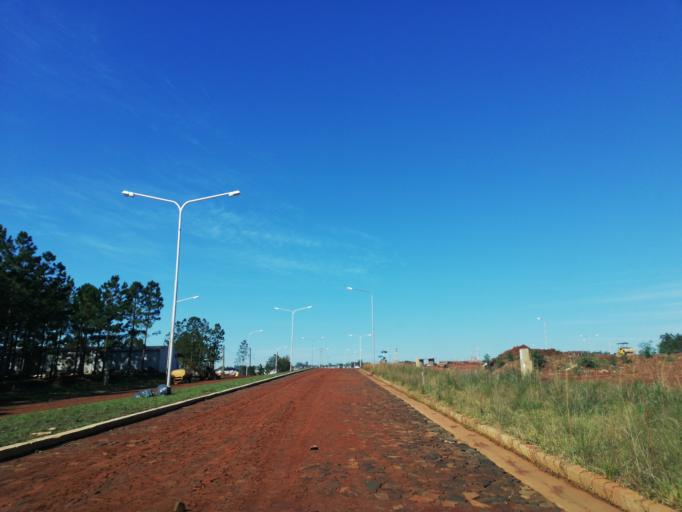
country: AR
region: Misiones
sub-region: Departamento de Capital
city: Posadas
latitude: -27.4063
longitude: -55.9944
